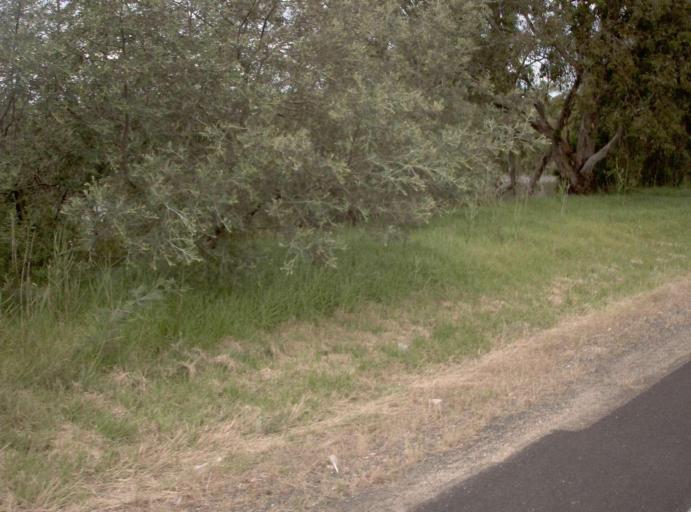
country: AU
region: Victoria
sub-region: East Gippsland
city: Bairnsdale
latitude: -37.8784
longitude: 147.6549
